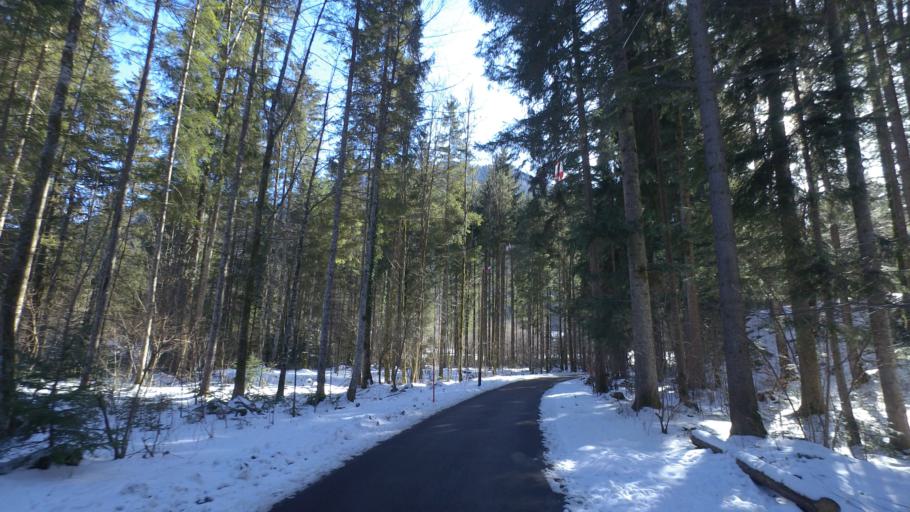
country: DE
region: Bavaria
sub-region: Upper Bavaria
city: Ruhpolding
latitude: 47.7444
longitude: 12.6143
